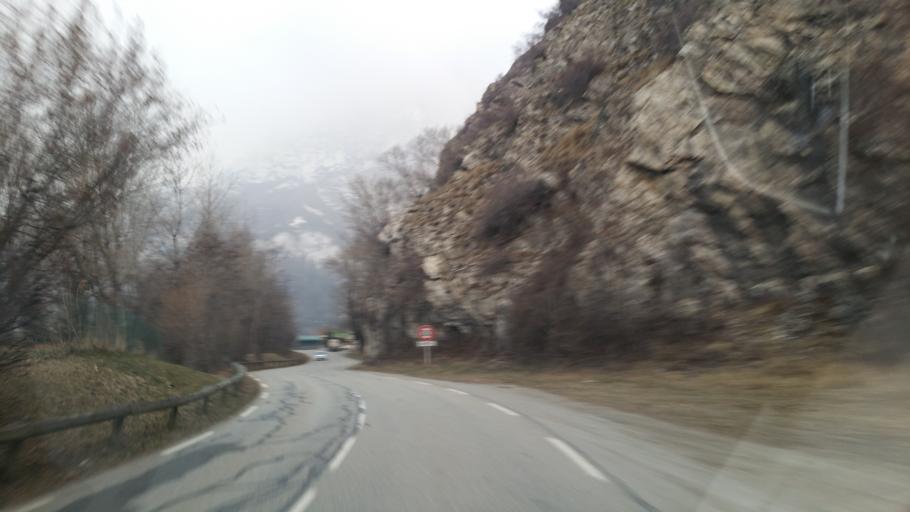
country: FR
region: Rhone-Alpes
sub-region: Departement de la Savoie
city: Villargondran
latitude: 45.2786
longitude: 6.3622
